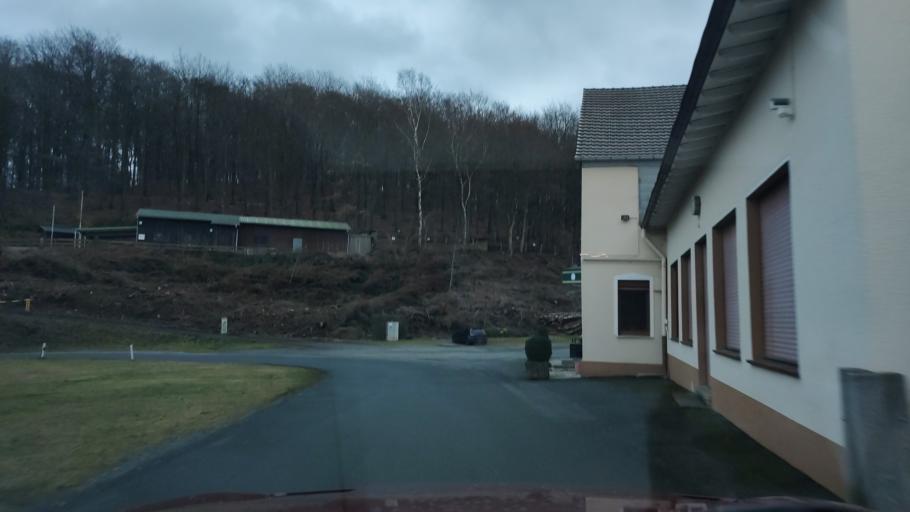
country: DE
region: North Rhine-Westphalia
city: Altena
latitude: 51.3252
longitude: 7.6823
